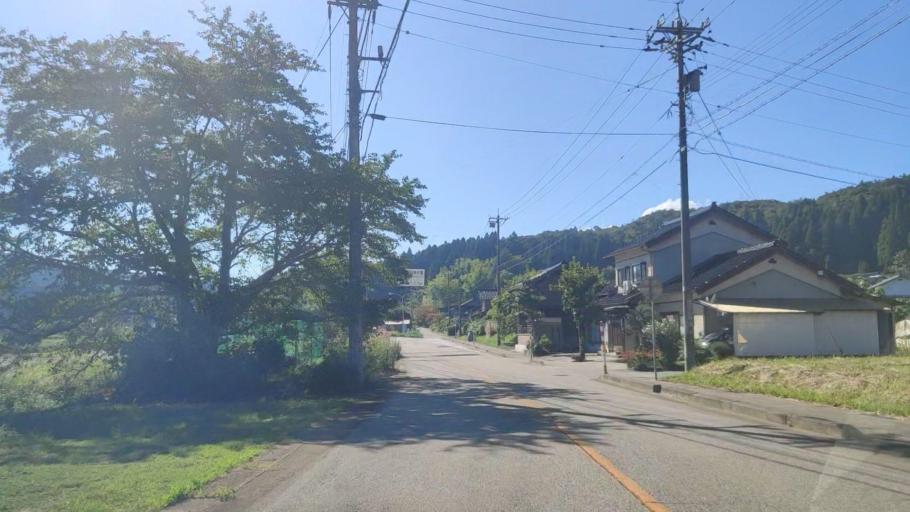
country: JP
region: Ishikawa
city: Nanao
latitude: 37.3374
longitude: 137.2128
